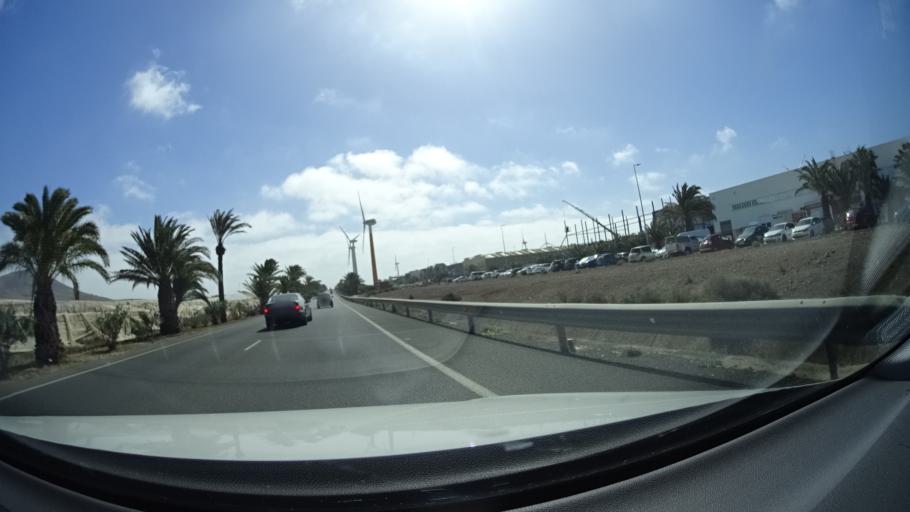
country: ES
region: Canary Islands
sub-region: Provincia de Las Palmas
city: Cruce de Arinaga
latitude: 27.8657
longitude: -15.4107
